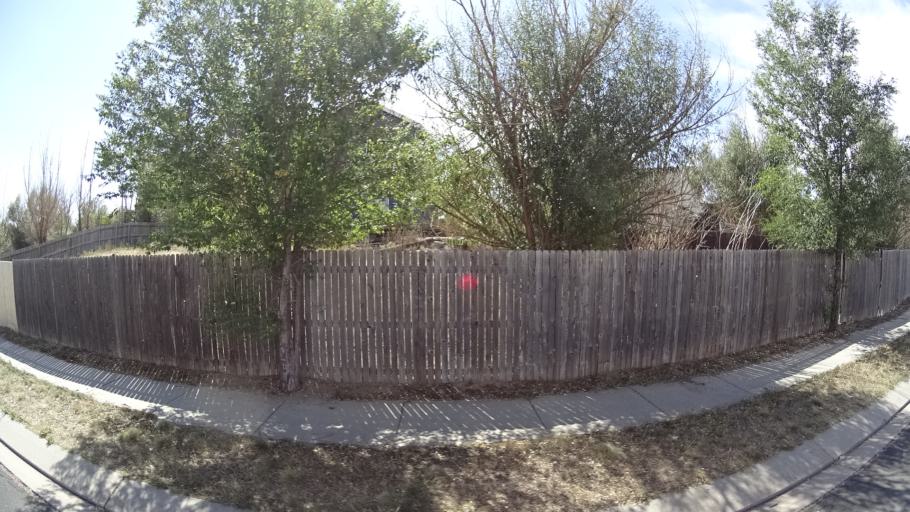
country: US
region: Colorado
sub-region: El Paso County
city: Cimarron Hills
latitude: 38.9054
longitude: -104.7127
